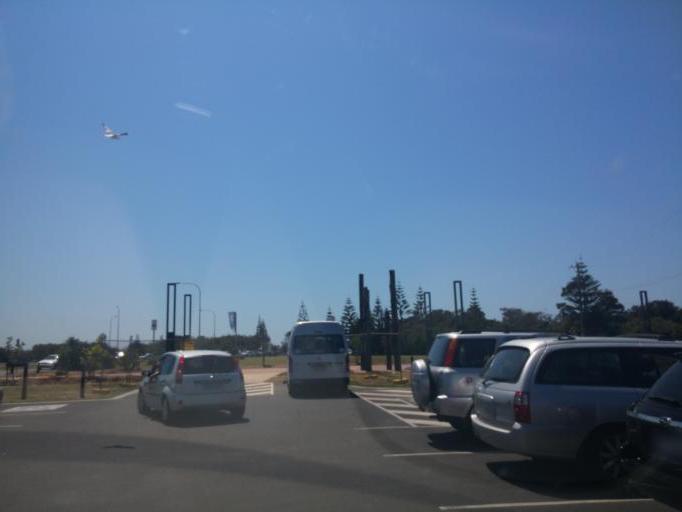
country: AU
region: New South Wales
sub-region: Coffs Harbour
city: Coffs Harbour
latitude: -30.3040
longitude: 153.1395
